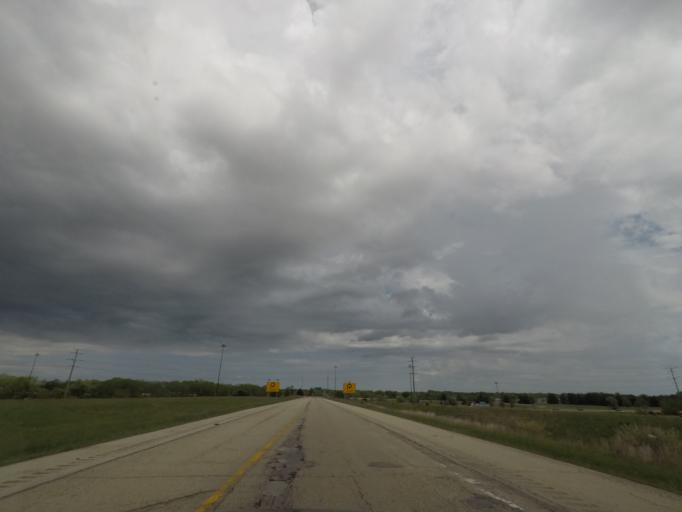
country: US
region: Illinois
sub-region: Winnebago County
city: Cherry Valley
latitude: 42.2174
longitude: -89.0113
